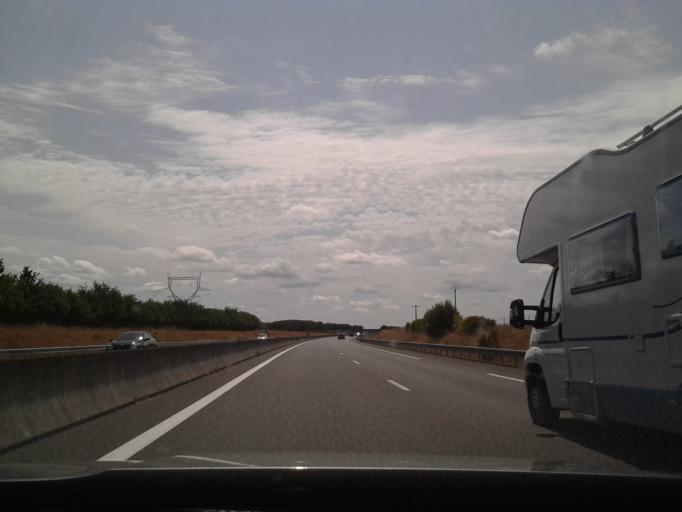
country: FR
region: Centre
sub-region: Departement d'Indre-et-Loire
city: Rouziers-de-Touraine
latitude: 47.5188
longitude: 0.6281
